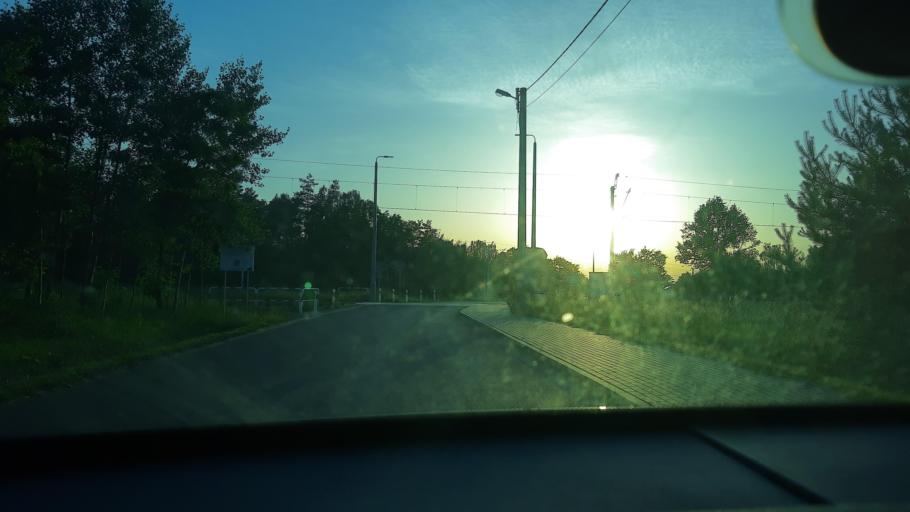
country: PL
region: Lodz Voivodeship
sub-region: Powiat zdunskowolski
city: Zdunska Wola
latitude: 51.6085
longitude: 18.9770
